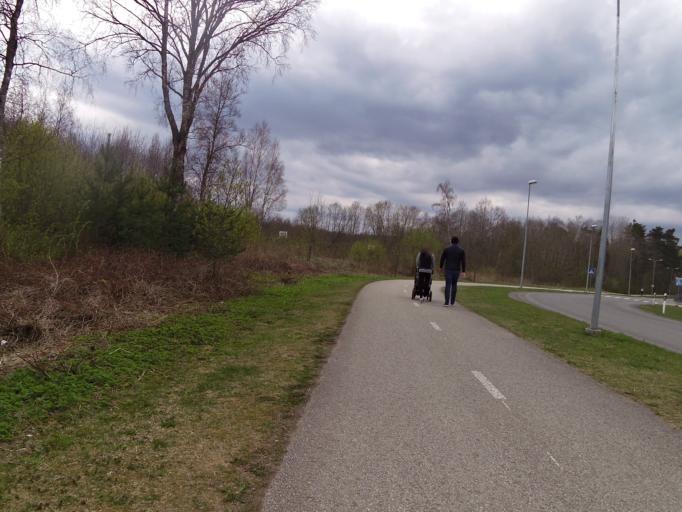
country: EE
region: Harju
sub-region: Kiili vald
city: Kiili
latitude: 59.3583
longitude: 24.8121
